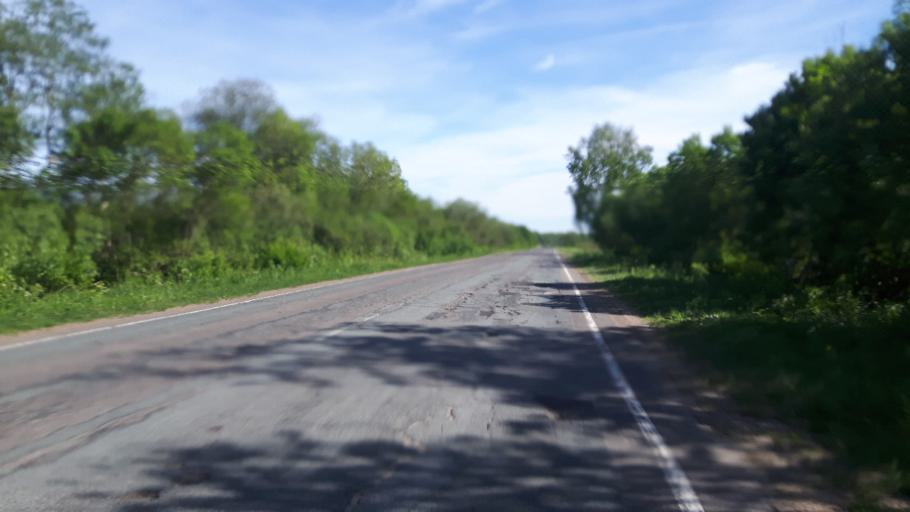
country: RU
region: Leningrad
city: Ivangorod
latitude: 59.4198
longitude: 28.3217
